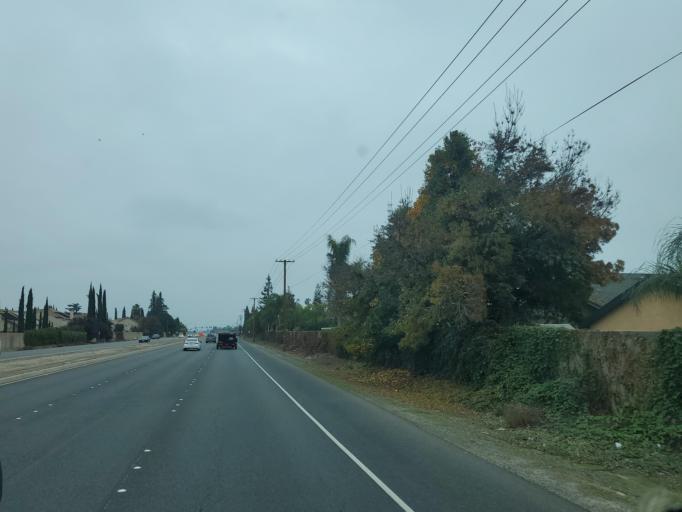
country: US
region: California
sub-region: Stanislaus County
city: Del Rio
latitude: 37.7004
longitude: -121.0279
